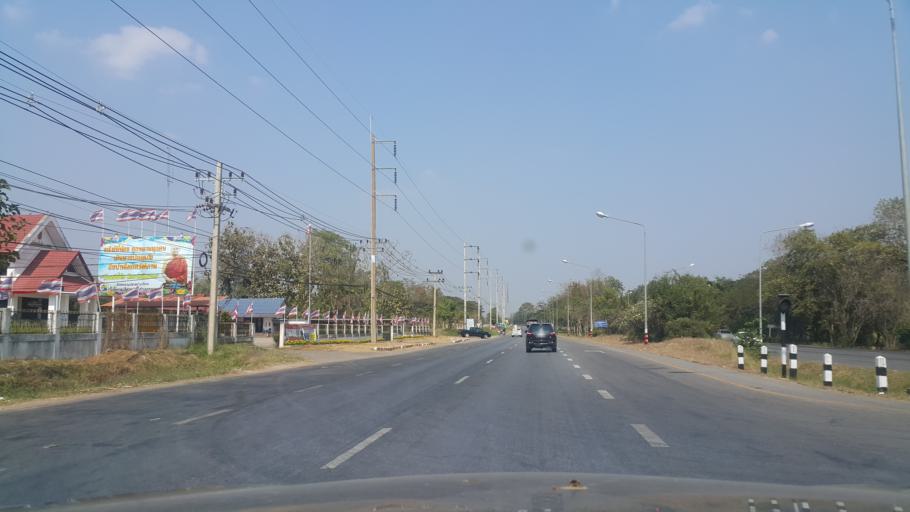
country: TH
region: Nakhon Ratchasima
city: Pak Thong Chai
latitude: 14.5904
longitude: 101.9987
